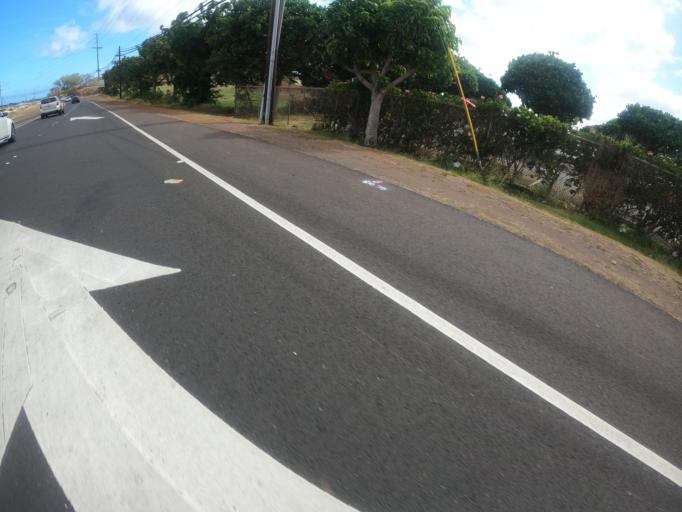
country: US
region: Hawaii
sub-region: Honolulu County
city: Makakilo City
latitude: 21.3390
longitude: -158.0752
